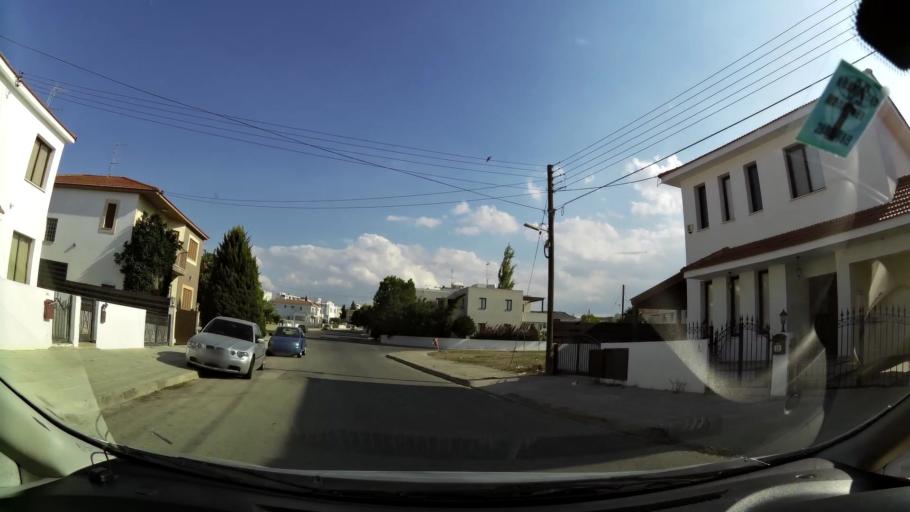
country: CY
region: Lefkosia
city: Nicosia
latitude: 35.1523
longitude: 33.2994
